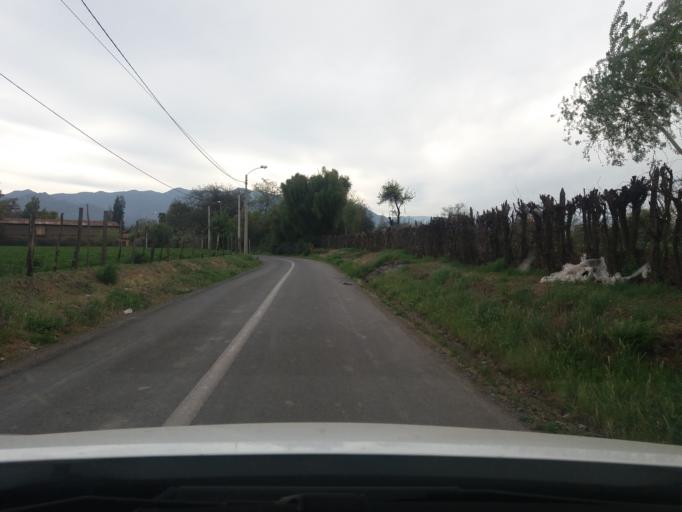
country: CL
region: Valparaiso
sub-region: Provincia de Los Andes
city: Los Andes
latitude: -32.8575
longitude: -70.6483
